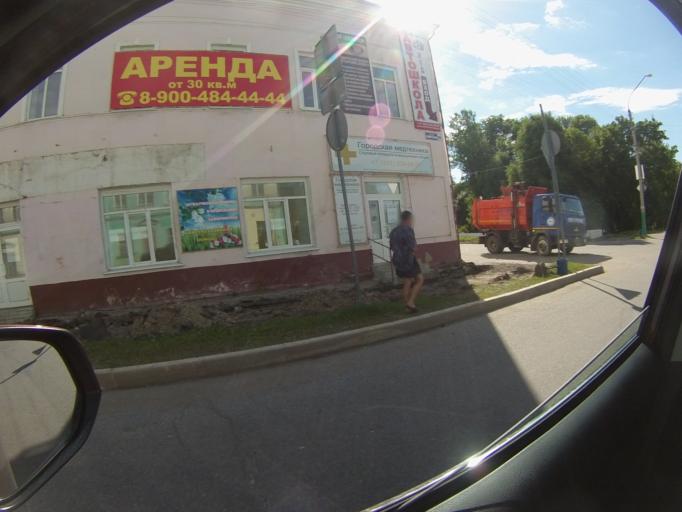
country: RU
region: Orjol
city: Mtsensk
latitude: 53.2813
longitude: 36.5696
